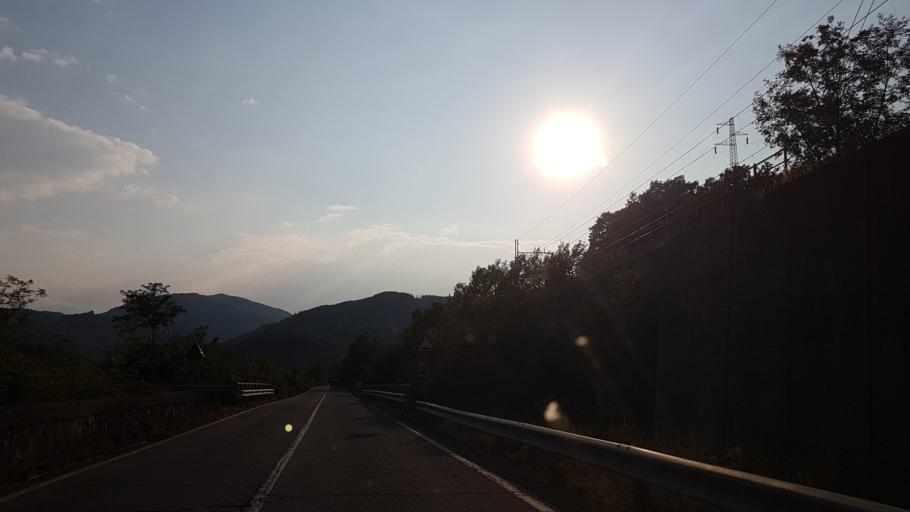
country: IT
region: Emilia-Romagna
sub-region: Provincia di Parma
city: Stazione Valmozzola
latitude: 44.5942
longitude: 9.9563
